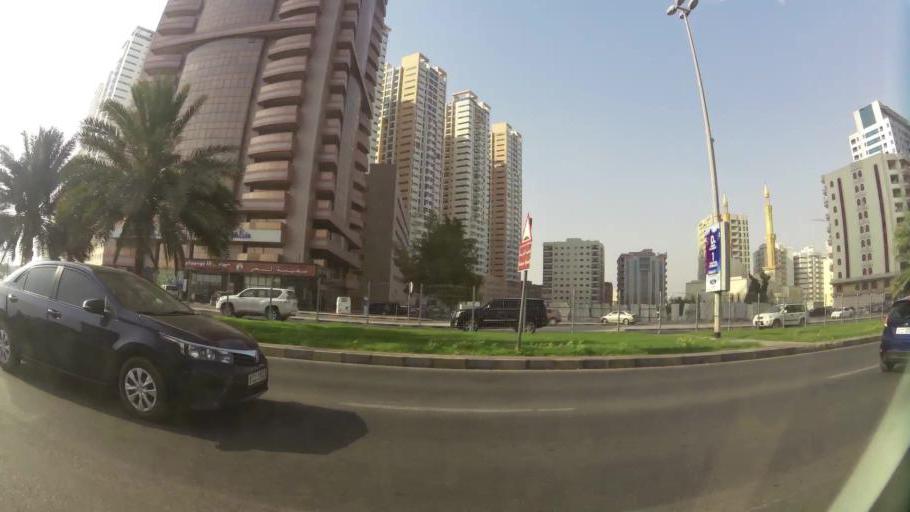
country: AE
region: Ajman
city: Ajman
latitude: 25.3927
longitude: 55.4313
